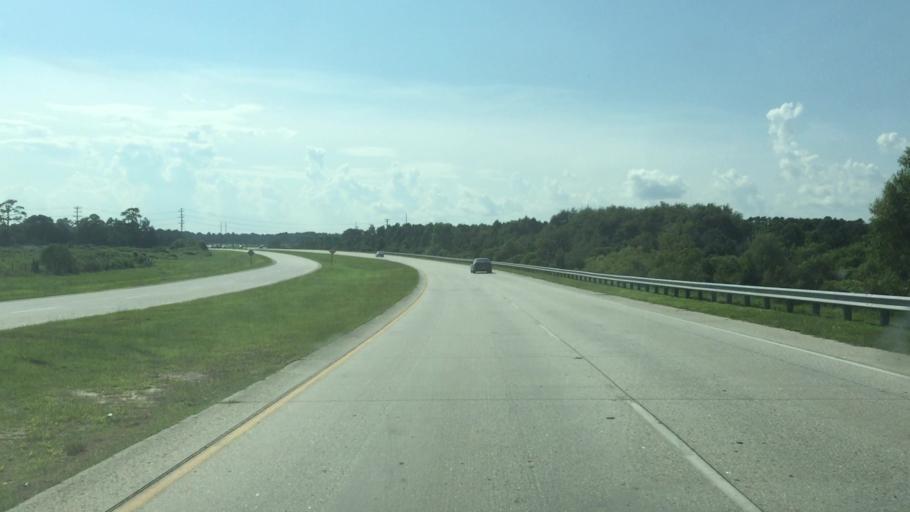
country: US
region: South Carolina
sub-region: Horry County
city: North Myrtle Beach
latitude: 33.8374
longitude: -78.6893
